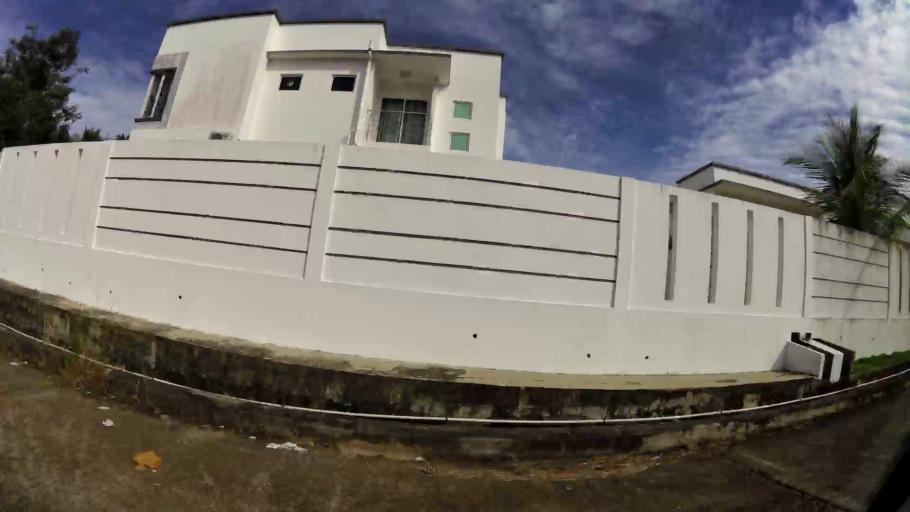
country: BN
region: Brunei and Muara
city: Bandar Seri Begawan
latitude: 4.8987
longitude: 114.9709
